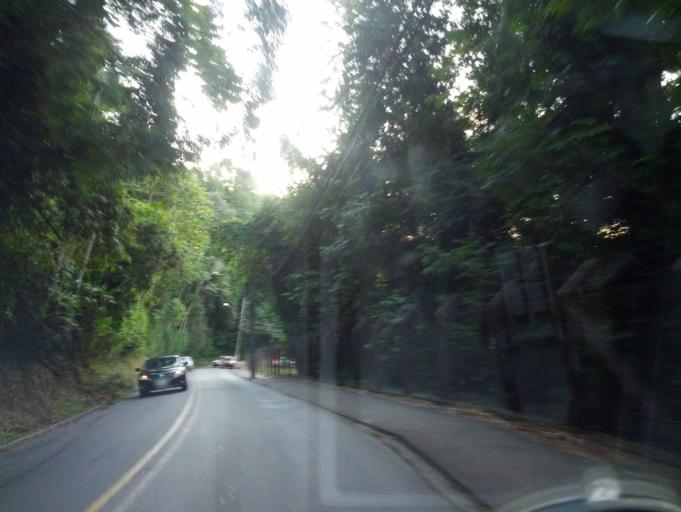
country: BR
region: Santa Catarina
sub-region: Blumenau
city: Blumenau
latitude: -26.9221
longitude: -49.0863
